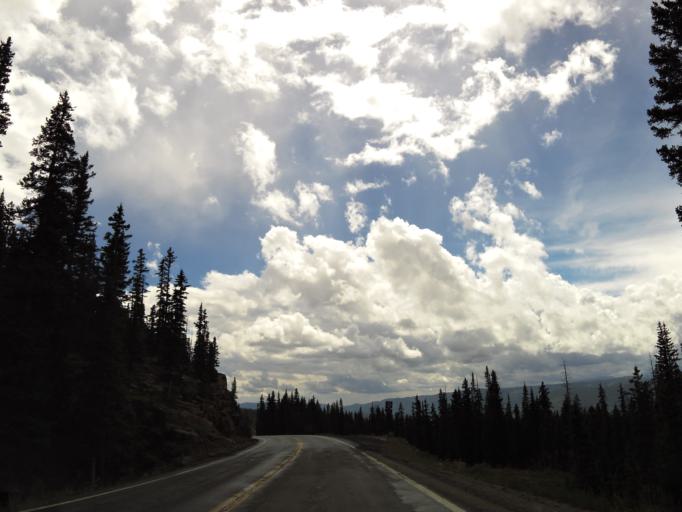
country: US
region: Colorado
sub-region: San Juan County
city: Silverton
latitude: 37.6907
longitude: -107.7796
